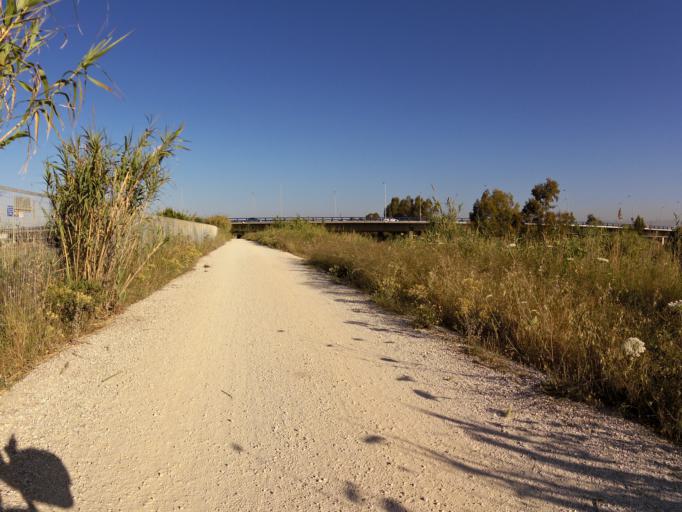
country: ES
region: Andalusia
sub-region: Provincia de Malaga
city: Torremolinos
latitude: 36.6727
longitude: -4.4642
